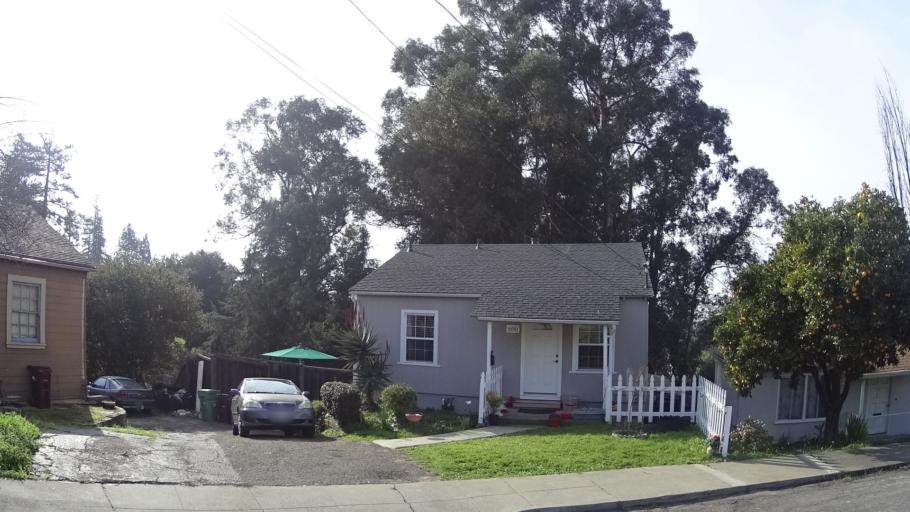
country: US
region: California
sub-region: Alameda County
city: Fairview
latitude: 37.6856
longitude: -122.0572
